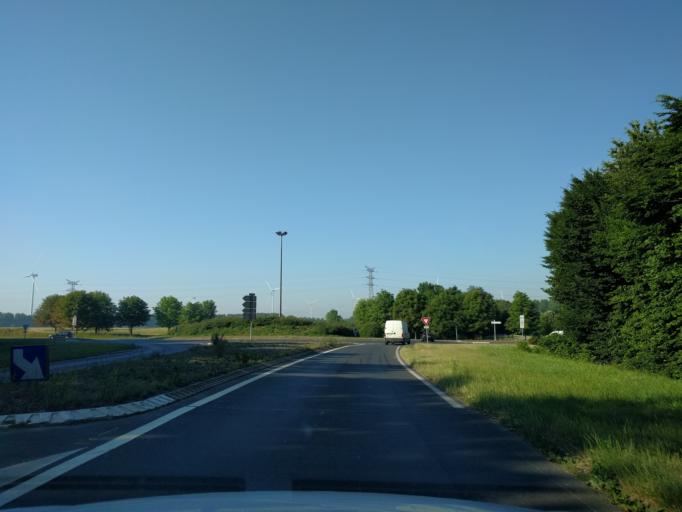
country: FR
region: Picardie
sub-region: Departement de la Somme
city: Roye
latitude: 49.6937
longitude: 2.8057
